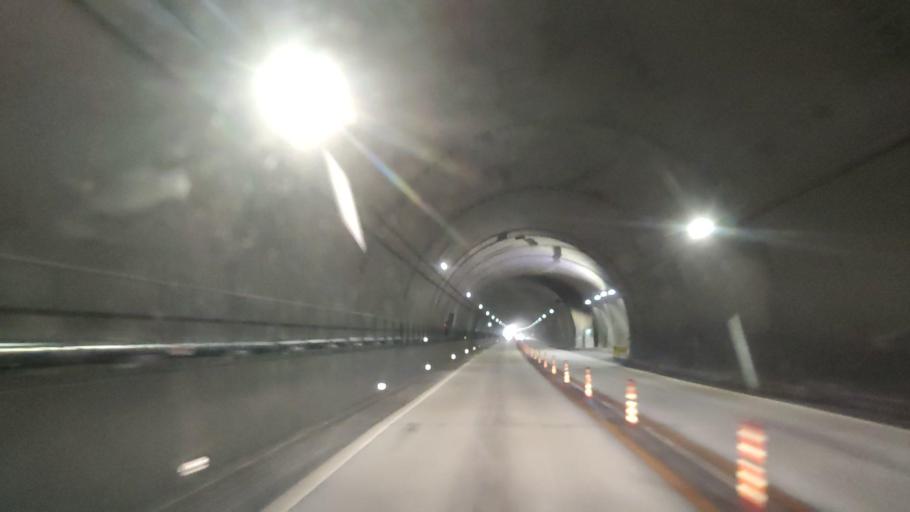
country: JP
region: Ehime
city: Hojo
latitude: 34.0836
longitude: 132.9774
